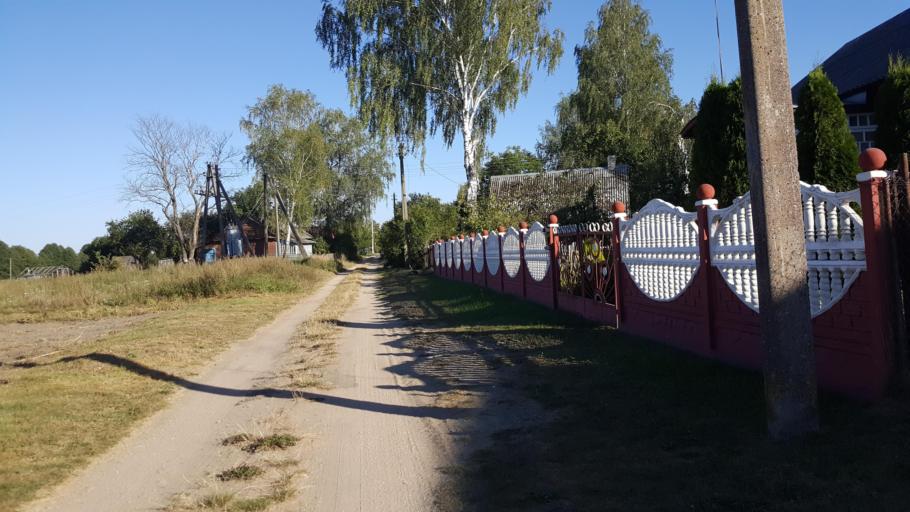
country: BY
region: Brest
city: Vysokaye
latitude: 52.3260
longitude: 23.2518
